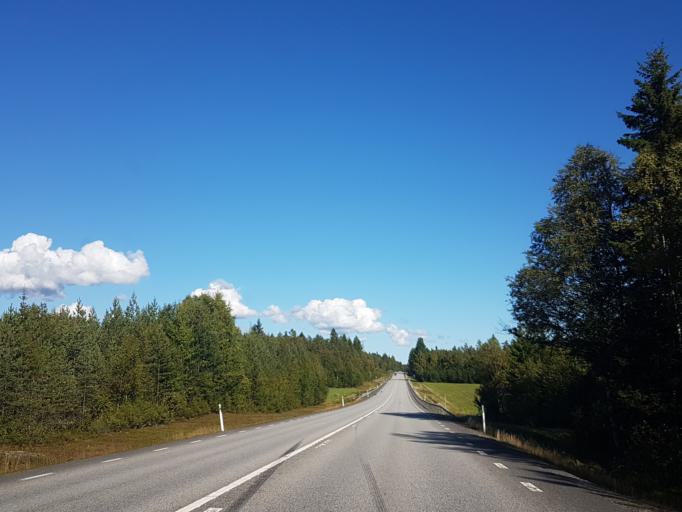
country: SE
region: Vaesterbotten
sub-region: Robertsfors Kommun
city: Robertsfors
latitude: 64.2439
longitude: 21.0322
